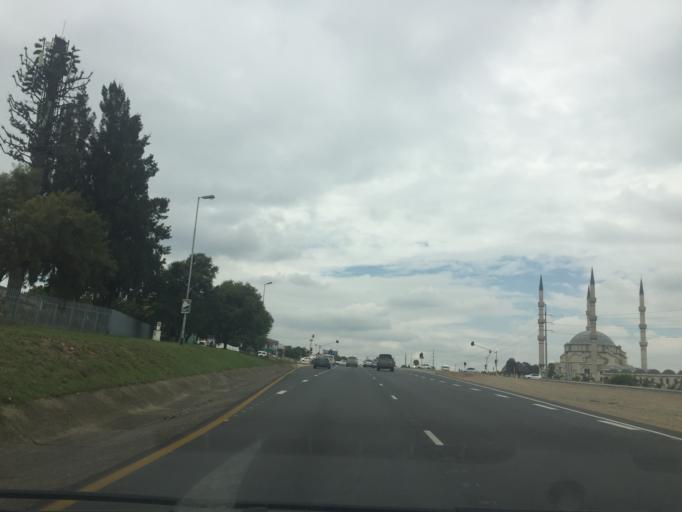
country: ZA
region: Gauteng
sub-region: City of Johannesburg Metropolitan Municipality
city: Midrand
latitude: -26.0155
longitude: 28.1264
